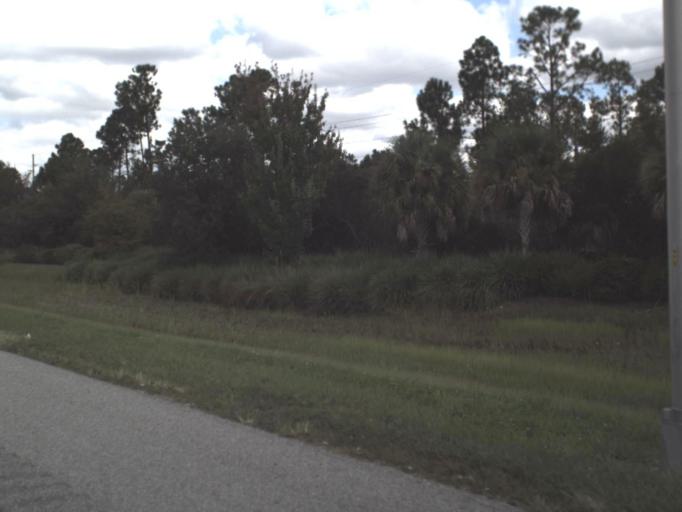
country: US
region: Florida
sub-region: Orange County
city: Sky Lake
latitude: 28.4403
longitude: -81.4139
